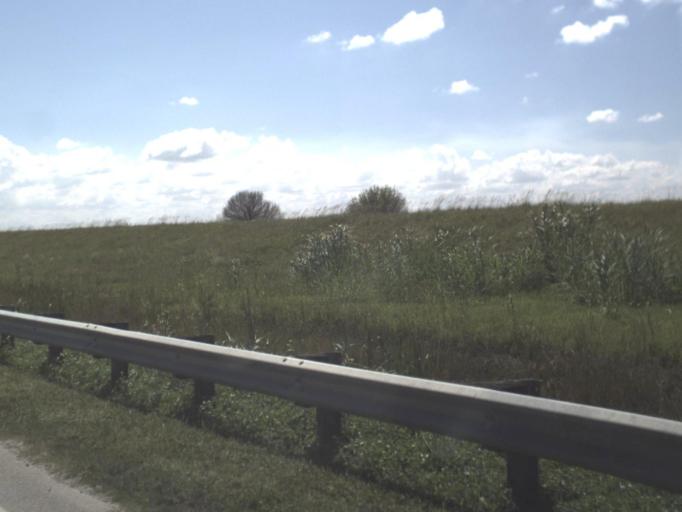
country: US
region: Florida
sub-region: Glades County
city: Moore Haven
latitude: 26.8819
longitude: -81.1226
